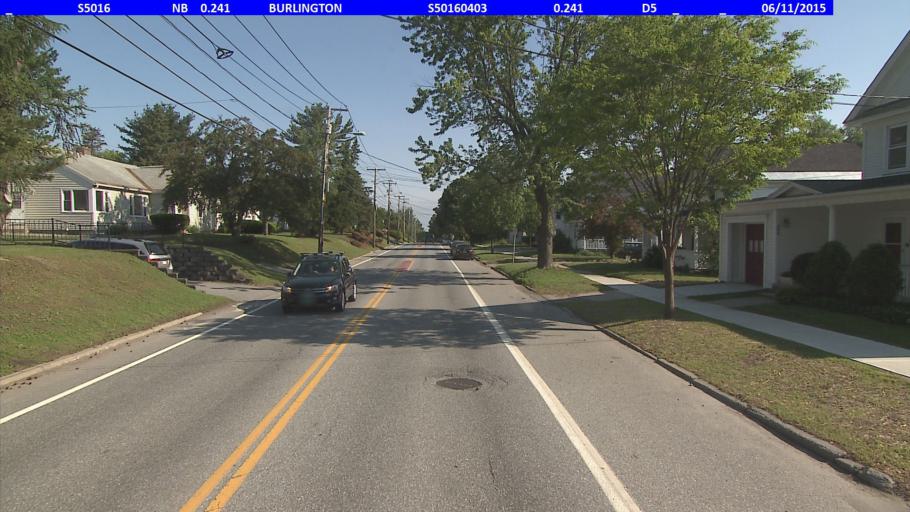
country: US
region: Vermont
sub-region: Chittenden County
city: Winooski
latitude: 44.4760
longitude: -73.1910
